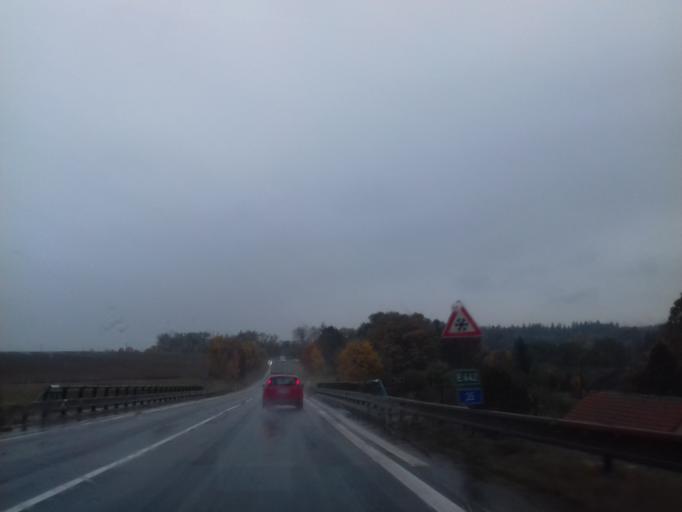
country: CZ
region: Pardubicky
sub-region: Okres Svitavy
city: Svitavy
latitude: 49.7714
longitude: 16.5214
